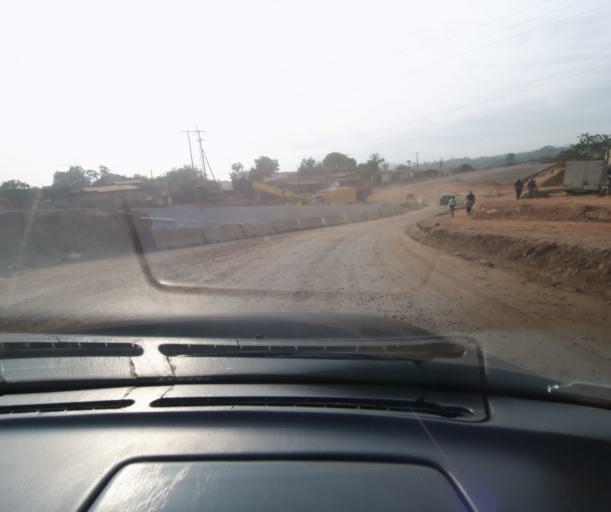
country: CM
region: Centre
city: Okoa
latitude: 3.9550
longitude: 11.5318
